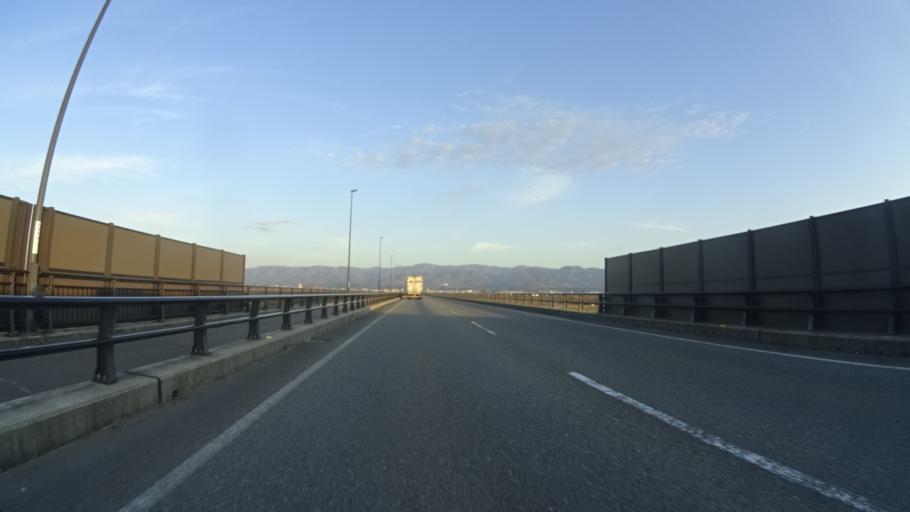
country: JP
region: Niigata
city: Nagaoka
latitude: 37.4330
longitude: 138.8143
